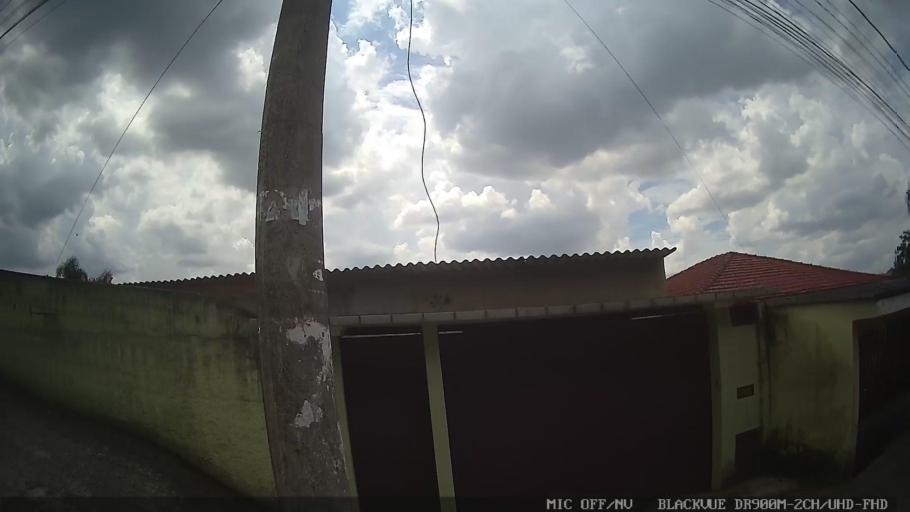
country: BR
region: Sao Paulo
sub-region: Ribeirao Pires
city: Ribeirao Pires
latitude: -23.7190
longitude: -46.4294
